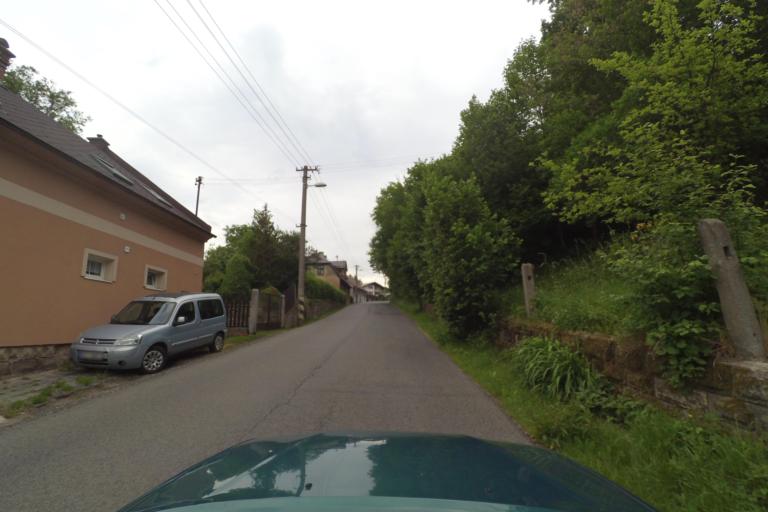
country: CZ
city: Cesky Dub
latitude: 50.6591
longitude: 14.9999
